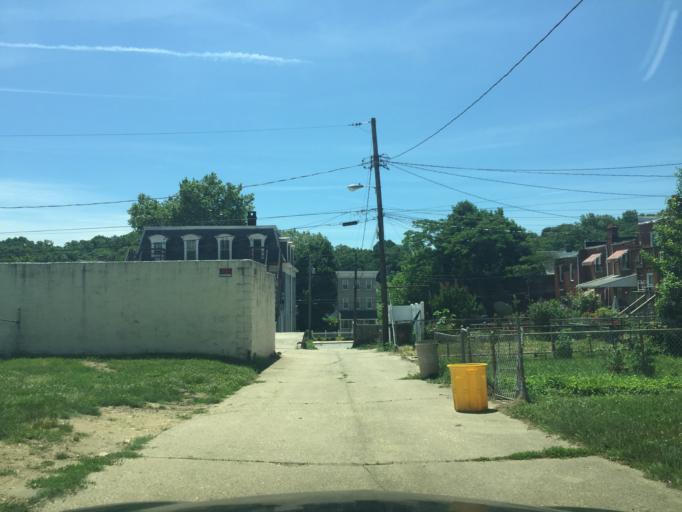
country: US
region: Maryland
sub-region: City of Baltimore
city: Baltimore
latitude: 39.3327
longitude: -76.6487
